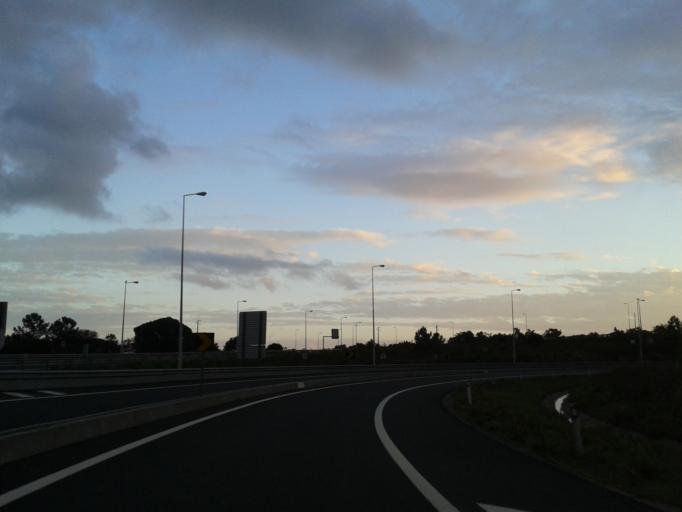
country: PT
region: Santarem
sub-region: Benavente
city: Poceirao
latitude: 38.8390
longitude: -8.7260
